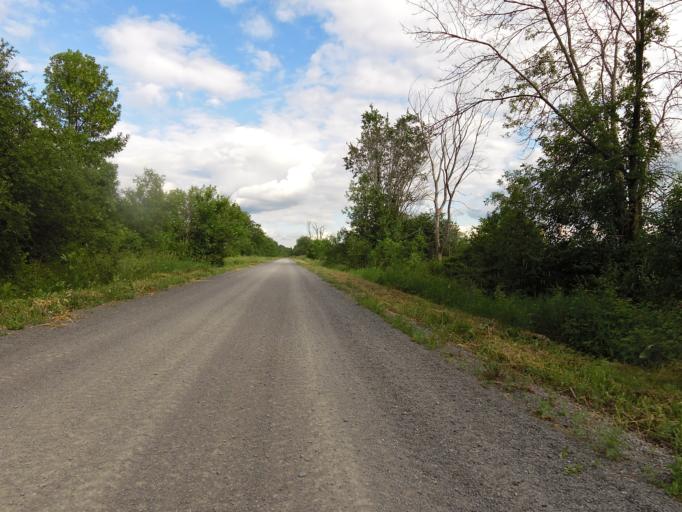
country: CA
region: Ontario
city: Arnprior
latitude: 45.3071
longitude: -76.2744
